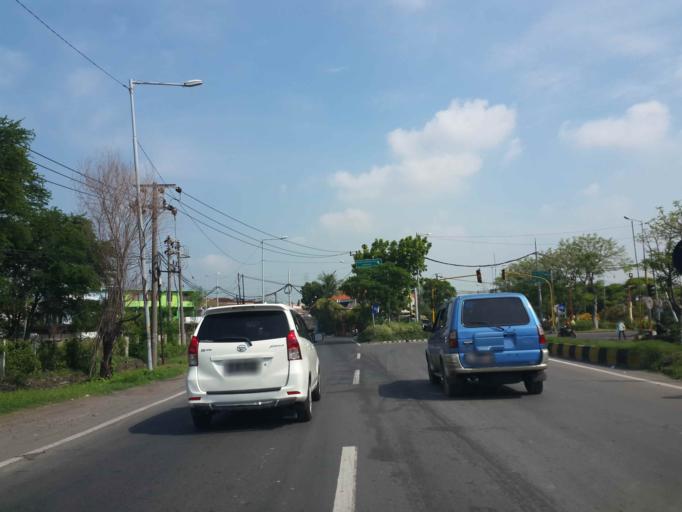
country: ID
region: East Java
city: Kebomas
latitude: -7.1970
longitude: 112.6458
